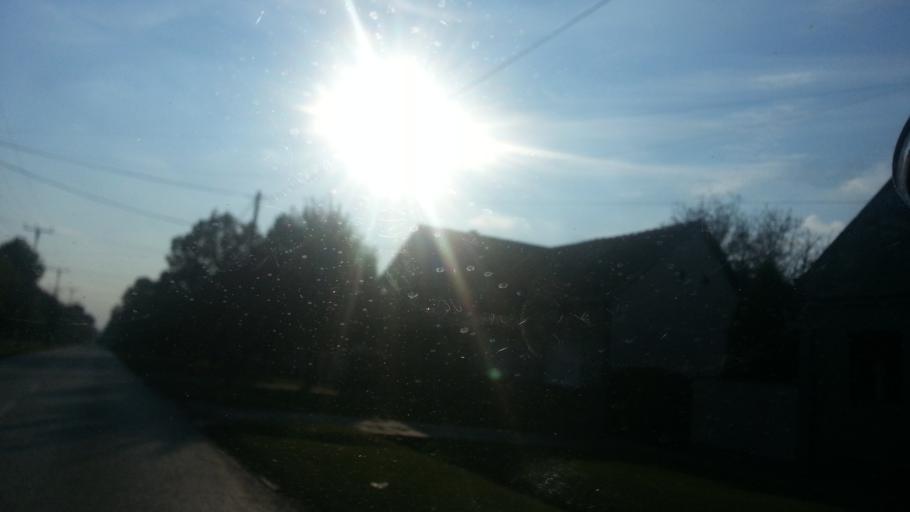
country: RS
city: Novi Slankamen
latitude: 45.1327
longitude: 20.2480
